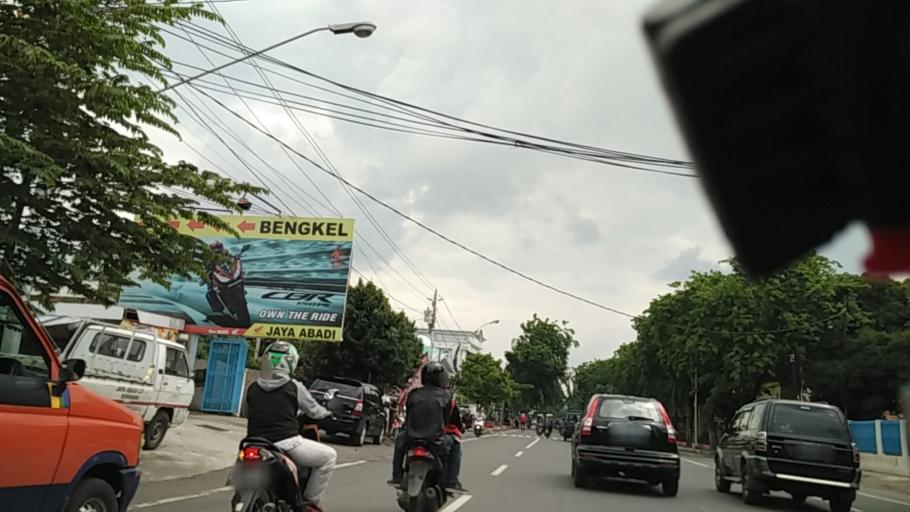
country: ID
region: Central Java
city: Semarang
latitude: -6.9856
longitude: 110.4348
